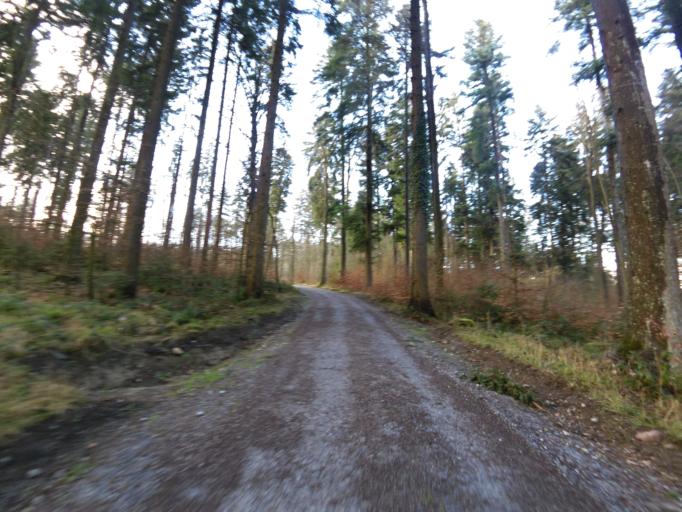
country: CH
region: Zurich
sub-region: Bezirk Dietikon
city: Uitikon
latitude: 47.3749
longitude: 8.4672
